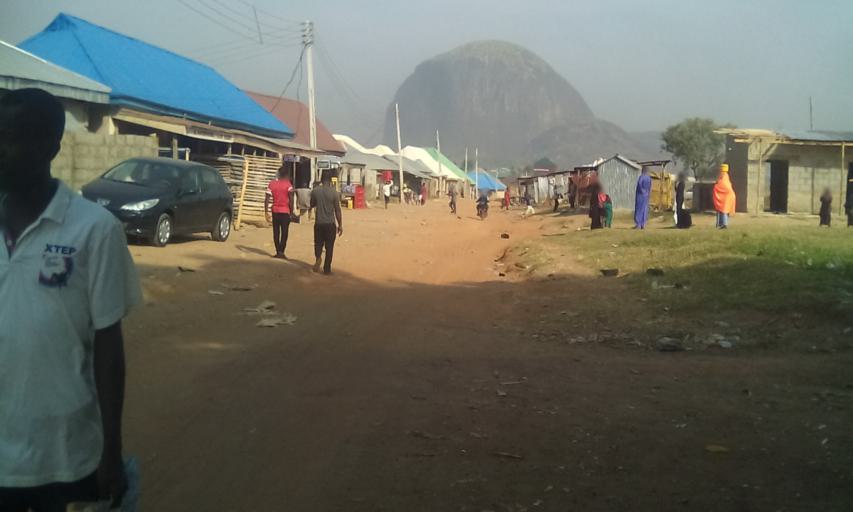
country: NG
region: Abuja Federal Capital Territory
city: Madala
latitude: 9.1082
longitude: 7.2418
